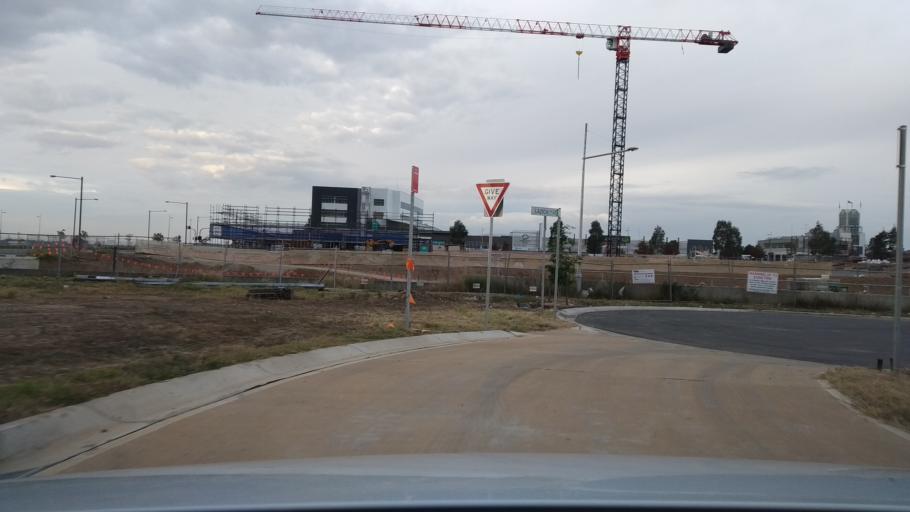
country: AU
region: New South Wales
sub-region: Camden
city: Narellan
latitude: -33.9996
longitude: 150.7374
